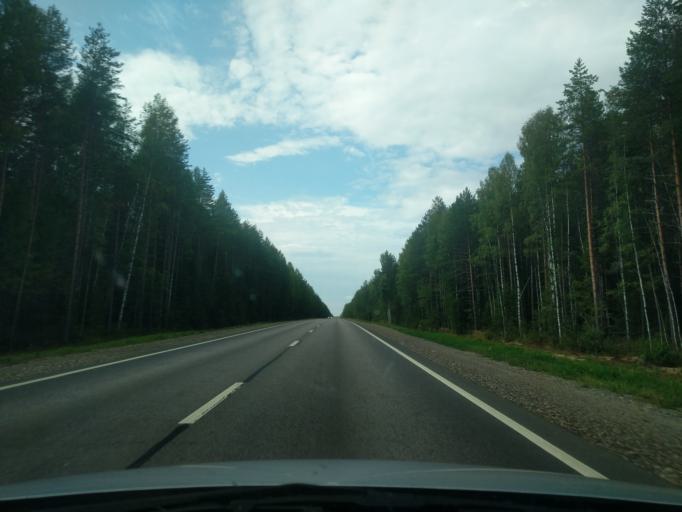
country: RU
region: Kostroma
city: Kadyy
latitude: 57.7957
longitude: 42.9294
